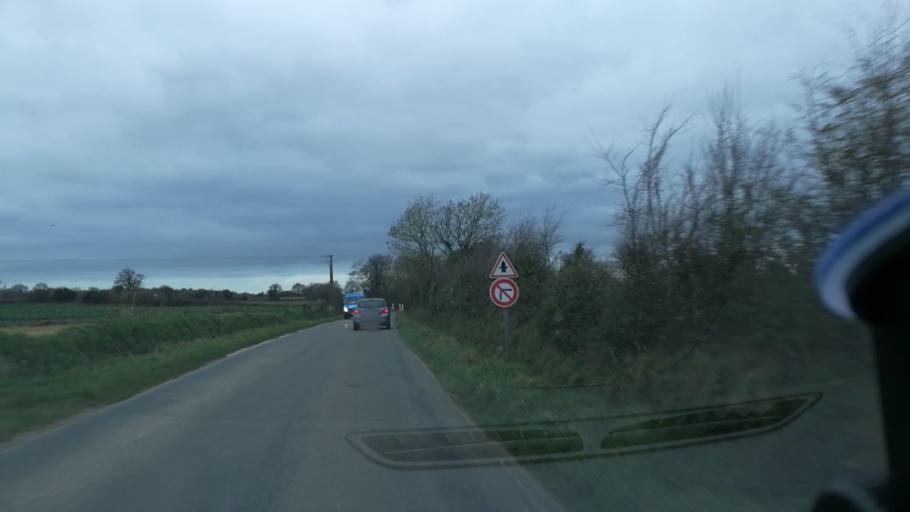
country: FR
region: Lower Normandy
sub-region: Departement de la Manche
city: Saint-Pierre-Eglise
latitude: 49.6596
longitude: -1.3981
